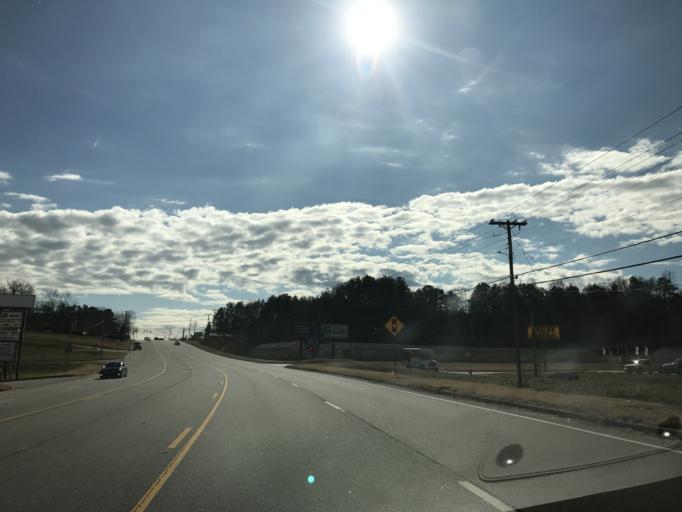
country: US
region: Georgia
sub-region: Paulding County
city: Hiram
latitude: 33.8690
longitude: -84.7648
